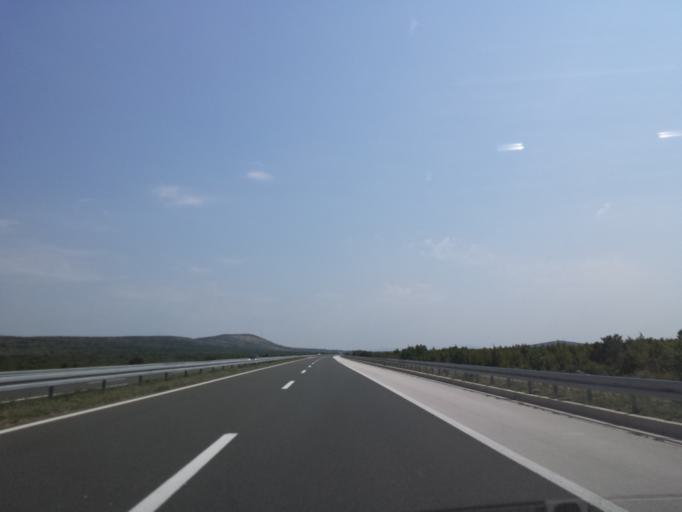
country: HR
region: Zadarska
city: Benkovac
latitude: 43.9557
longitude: 15.6753
